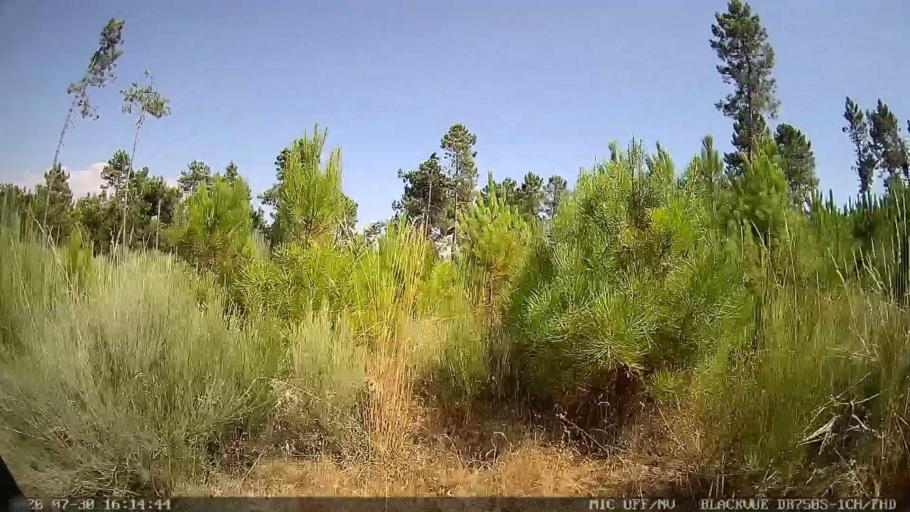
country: PT
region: Vila Real
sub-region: Murca
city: Murca
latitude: 41.3353
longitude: -7.4812
